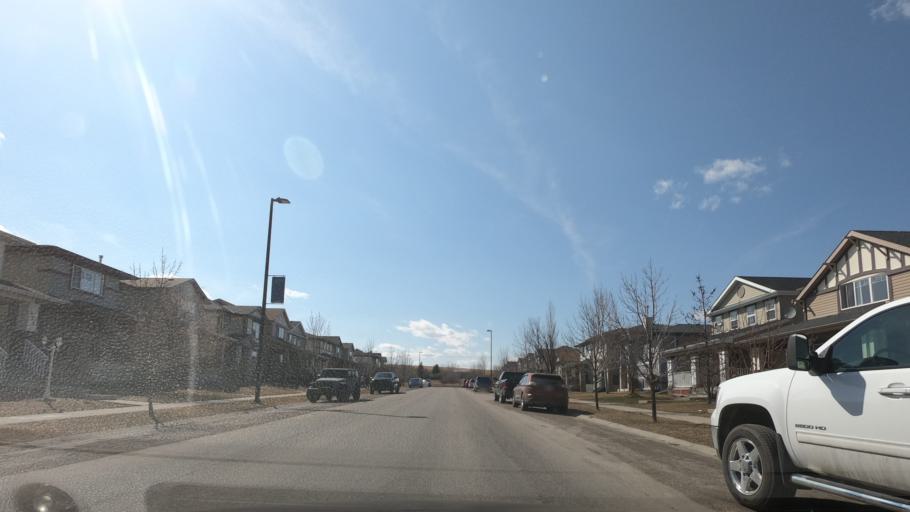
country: CA
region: Alberta
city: Airdrie
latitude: 51.2883
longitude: -114.0461
